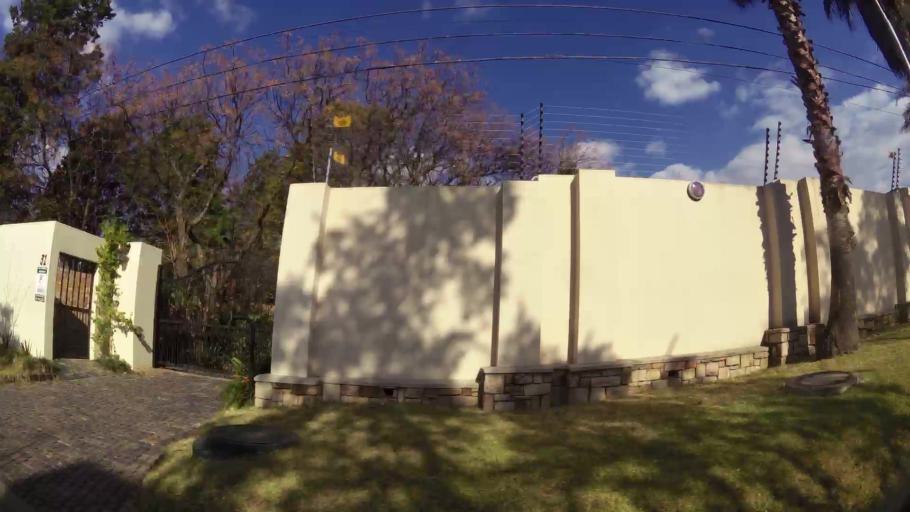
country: ZA
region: Gauteng
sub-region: City of Johannesburg Metropolitan Municipality
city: Diepsloot
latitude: -26.0217
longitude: 28.0256
